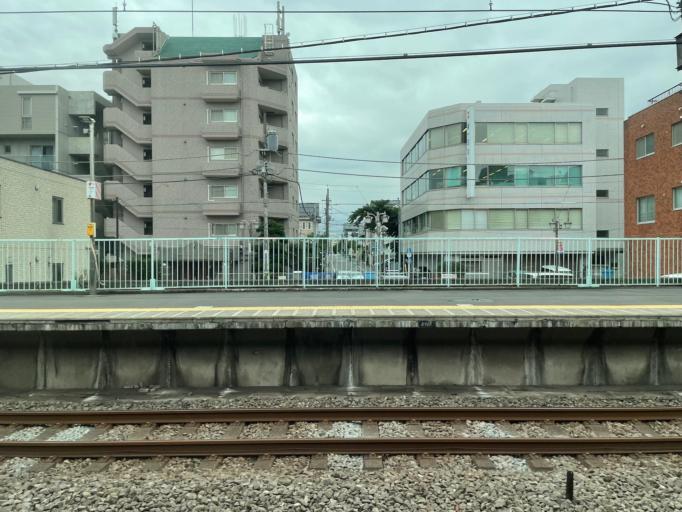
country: JP
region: Tokyo
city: Musashino
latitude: 35.7246
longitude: 139.6159
